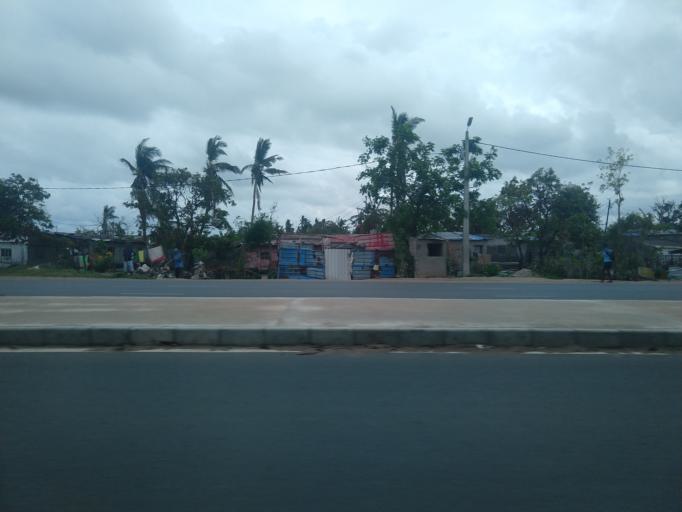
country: MZ
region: Sofala
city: Beira
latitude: -19.7853
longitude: 34.8765
